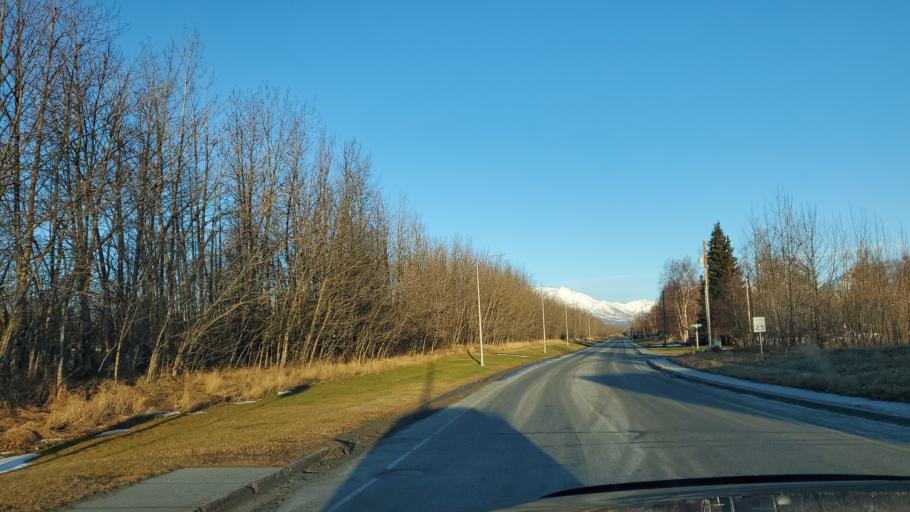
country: US
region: Alaska
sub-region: Matanuska-Susitna Borough
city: Palmer
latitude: 61.6068
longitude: -149.1101
